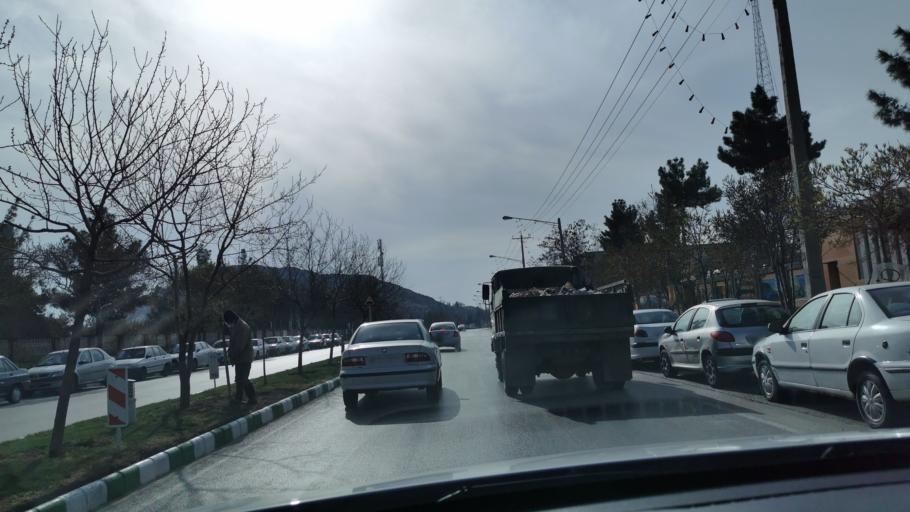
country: IR
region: Razavi Khorasan
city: Mashhad
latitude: 36.2817
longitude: 59.5525
